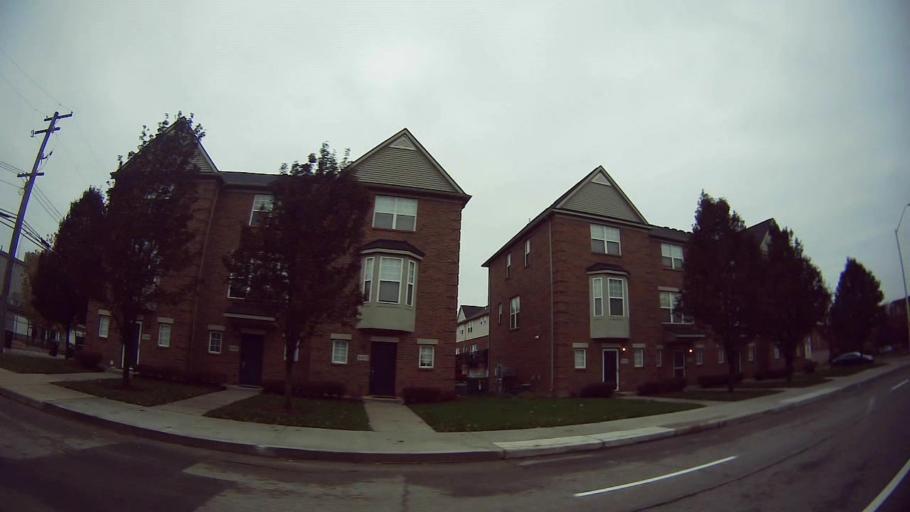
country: US
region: Michigan
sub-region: Wayne County
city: Hamtramck
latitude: 42.3636
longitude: -83.0630
